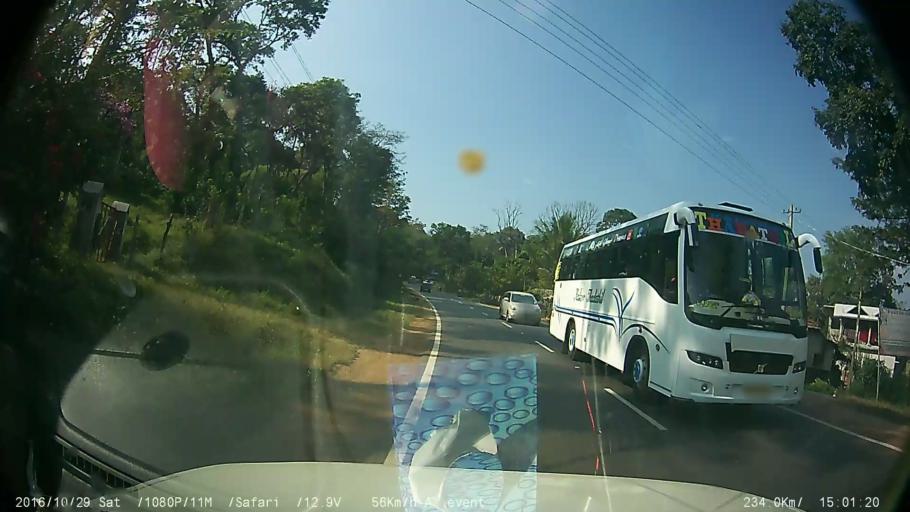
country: IN
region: Karnataka
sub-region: Kodagu
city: Suntikoppa
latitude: 12.4413
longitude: 75.8496
